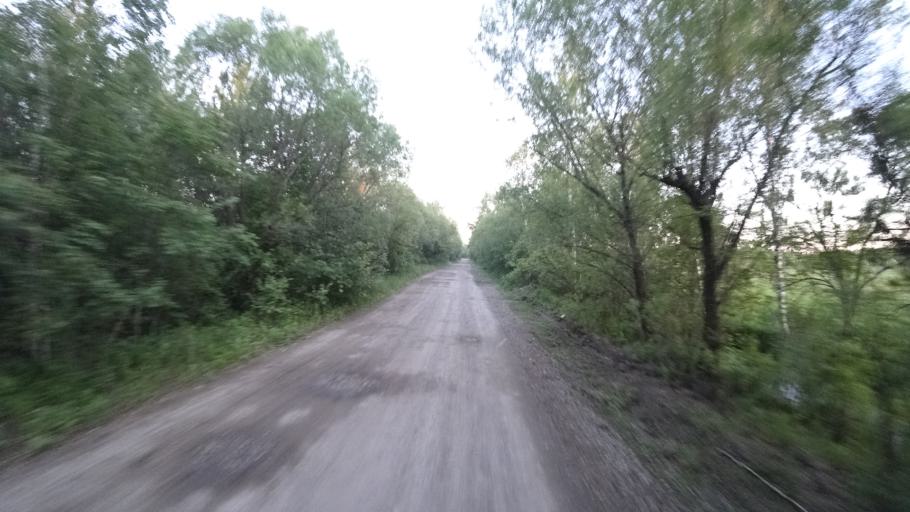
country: RU
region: Khabarovsk Krai
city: Khor
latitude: 47.8469
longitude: 134.9484
